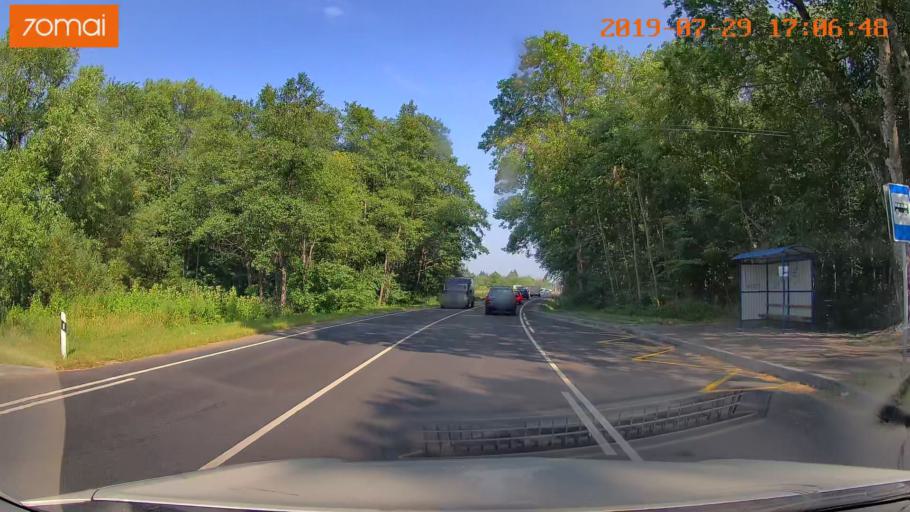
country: RU
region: Kaliningrad
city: Vzmorye
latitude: 54.8191
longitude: 20.3131
